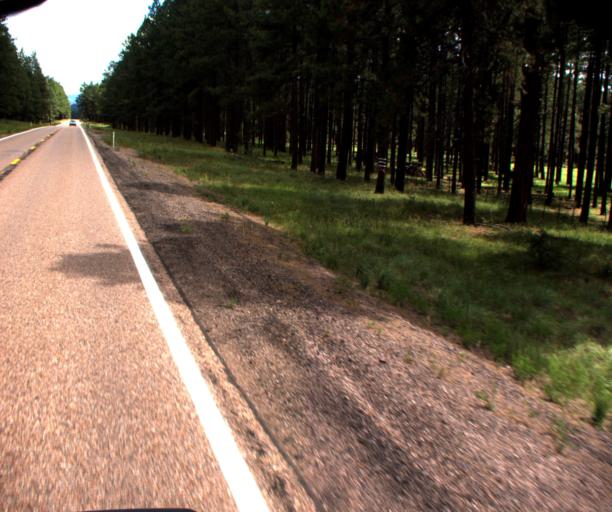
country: US
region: Arizona
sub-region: Navajo County
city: Pinetop-Lakeside
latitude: 34.0601
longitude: -109.7666
